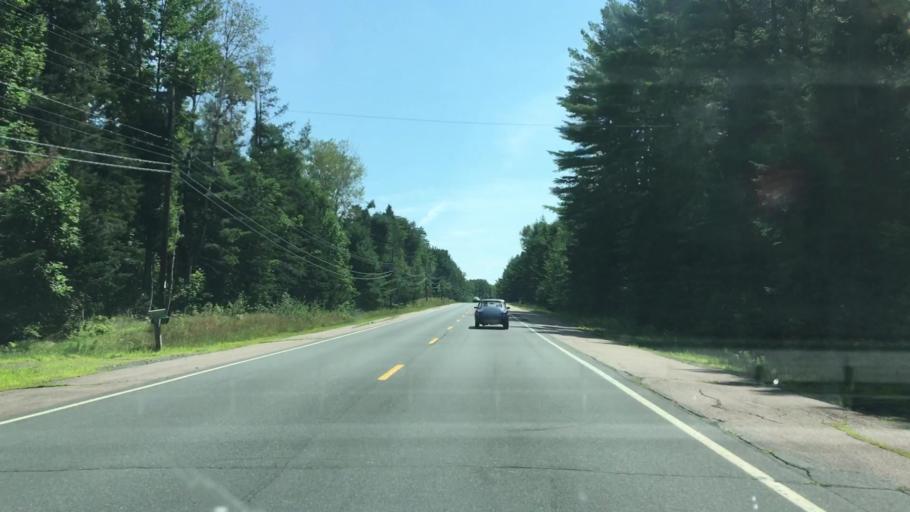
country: US
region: Maine
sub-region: Washington County
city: Calais
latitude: 45.1636
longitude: -67.2024
